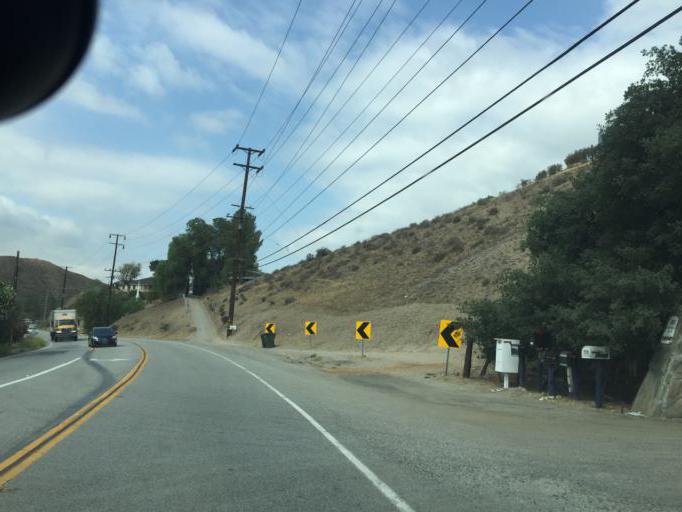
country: US
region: California
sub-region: Los Angeles County
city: Santa Clarita
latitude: 34.4634
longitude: -118.4825
